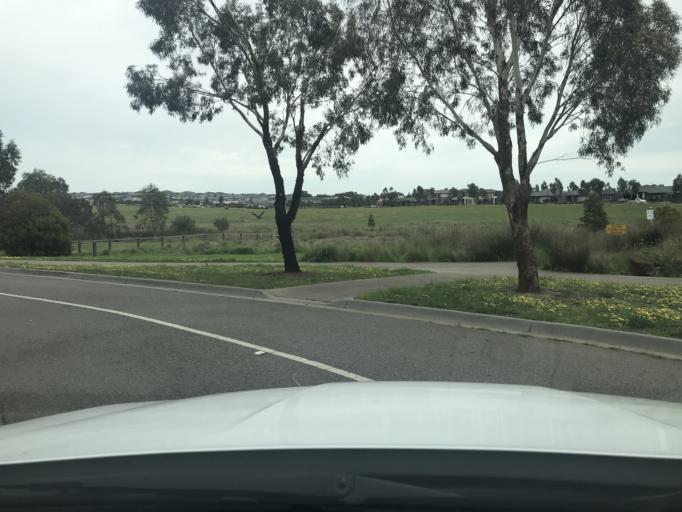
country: AU
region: Victoria
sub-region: Hume
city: Roxburgh Park
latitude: -37.5932
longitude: 144.9030
